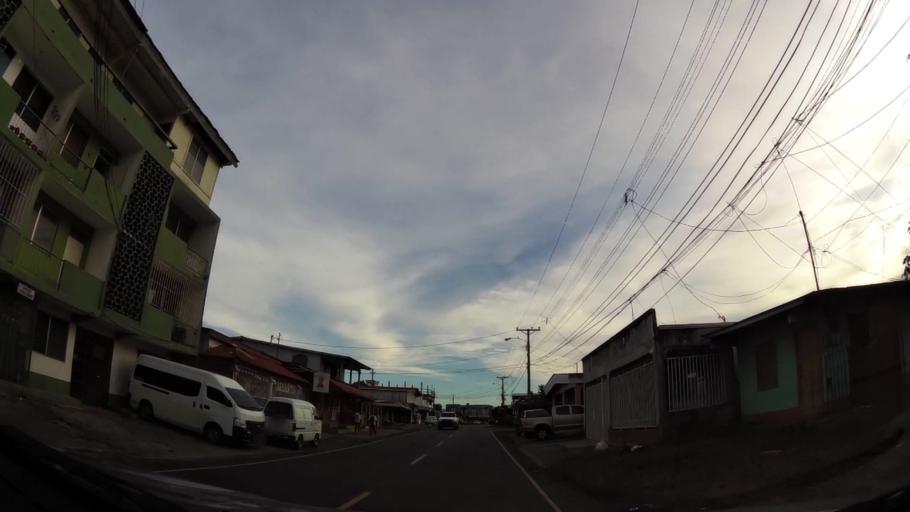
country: PA
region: Panama
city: La Chorrera
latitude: 8.8851
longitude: -79.7811
